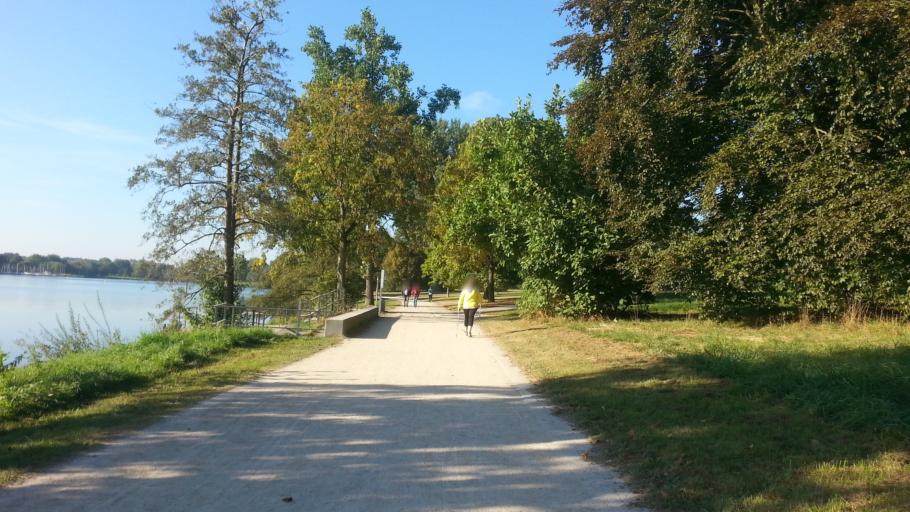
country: DE
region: North Rhine-Westphalia
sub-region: Regierungsbezirk Munster
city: Muenster
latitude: 51.9494
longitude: 7.6013
